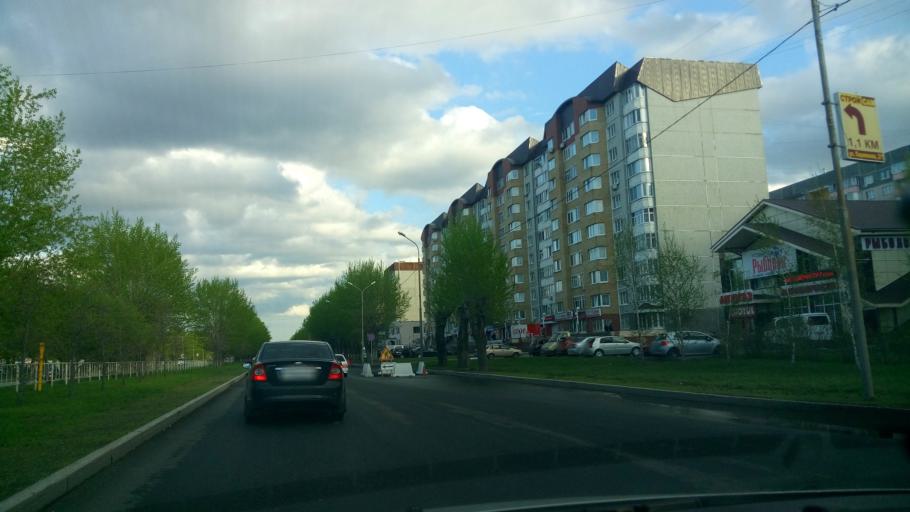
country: RU
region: Tjumen
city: Tyumen
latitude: 57.1374
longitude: 65.5970
